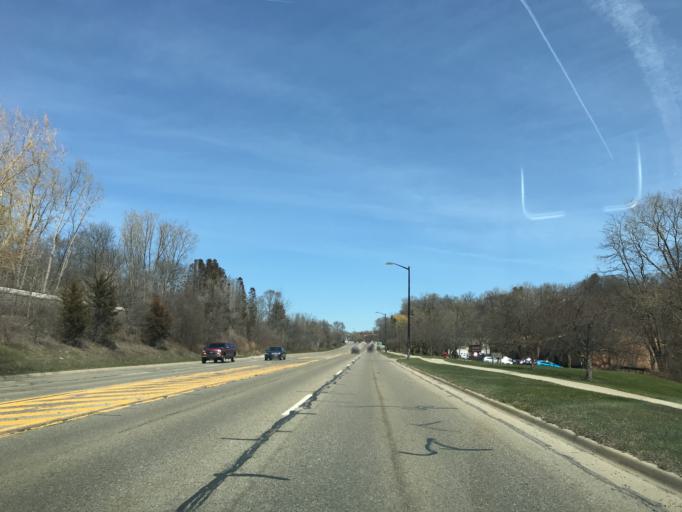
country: US
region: Michigan
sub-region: Washtenaw County
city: Ann Arbor
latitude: 42.2936
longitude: -83.7346
